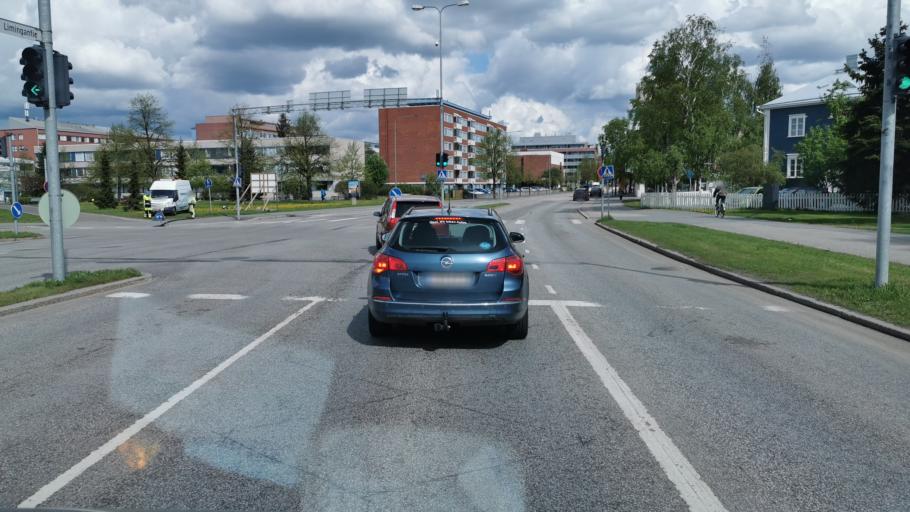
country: FI
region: Northern Ostrobothnia
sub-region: Oulu
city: Oulu
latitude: 65.0036
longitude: 25.4639
